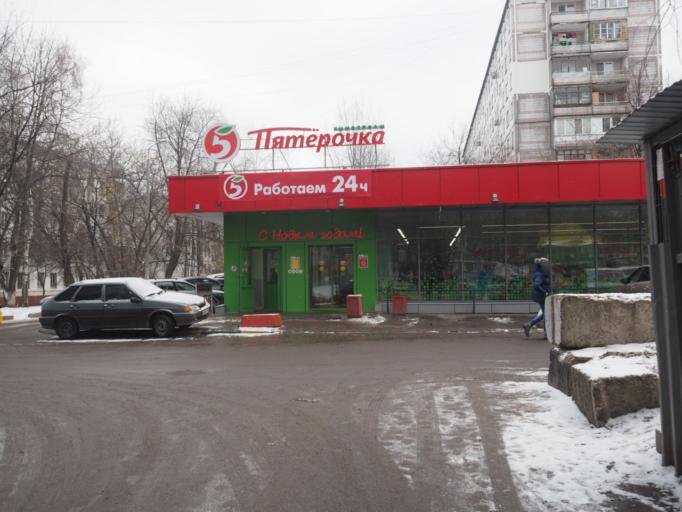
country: RU
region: Moscow
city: Orekhovo-Borisovo Severnoye
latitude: 55.6325
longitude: 37.6800
